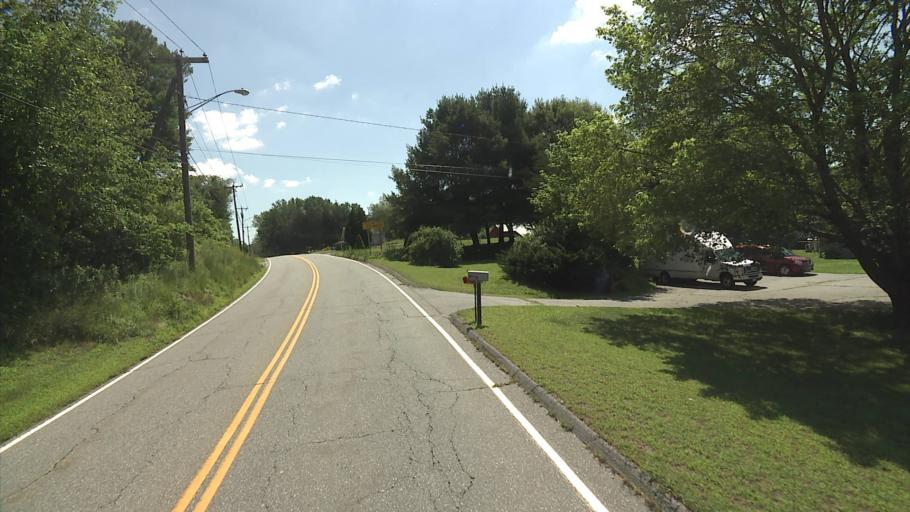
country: US
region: Connecticut
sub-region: Windham County
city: Plainfield Village
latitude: 41.6865
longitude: -71.9418
